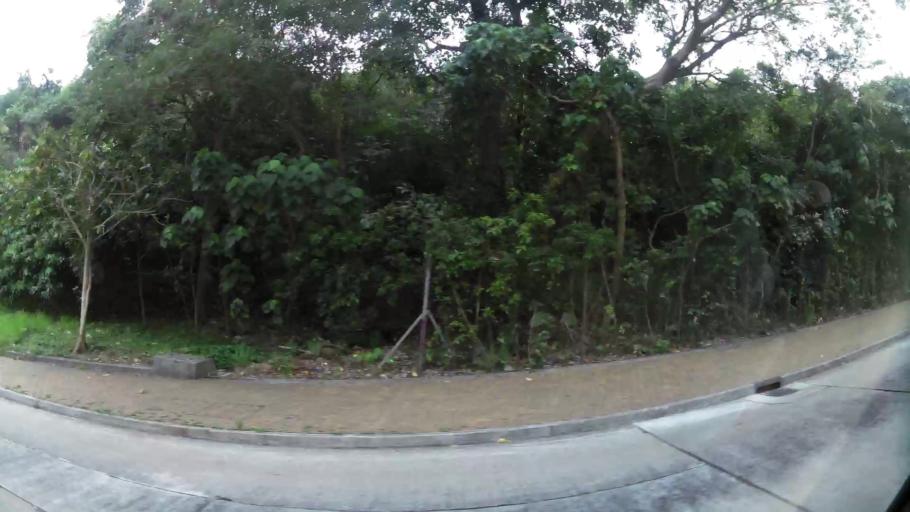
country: HK
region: Wanchai
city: Wan Chai
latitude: 22.2721
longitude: 114.2330
